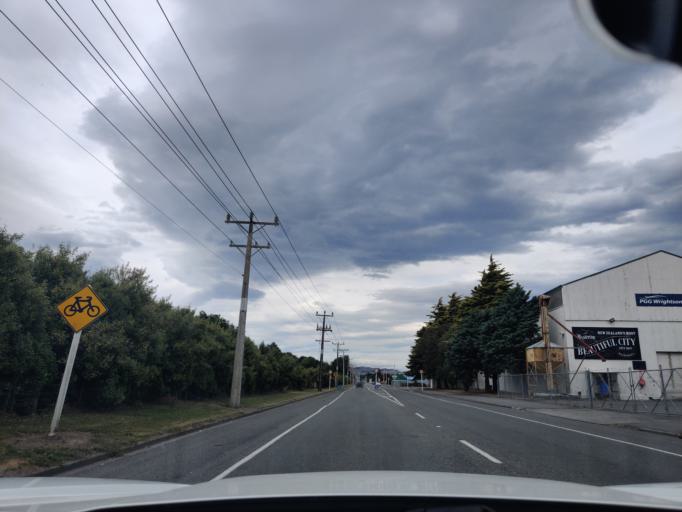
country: NZ
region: Wellington
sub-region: Masterton District
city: Masterton
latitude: -40.9501
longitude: 175.6316
